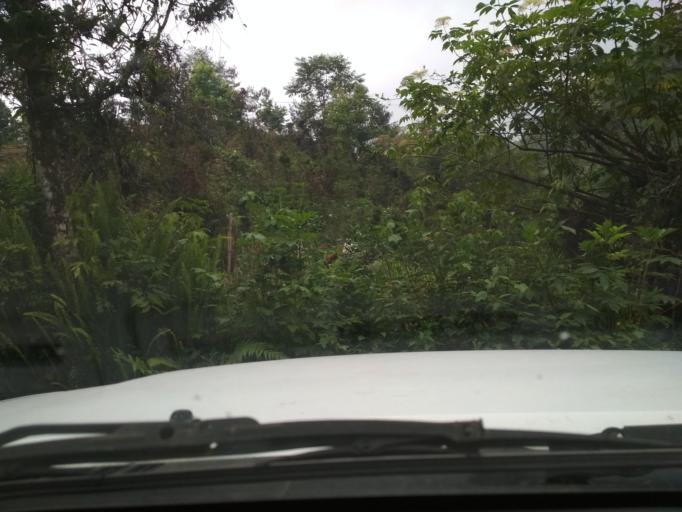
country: MX
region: Veracruz
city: La Perla
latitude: 18.9308
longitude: -97.1455
